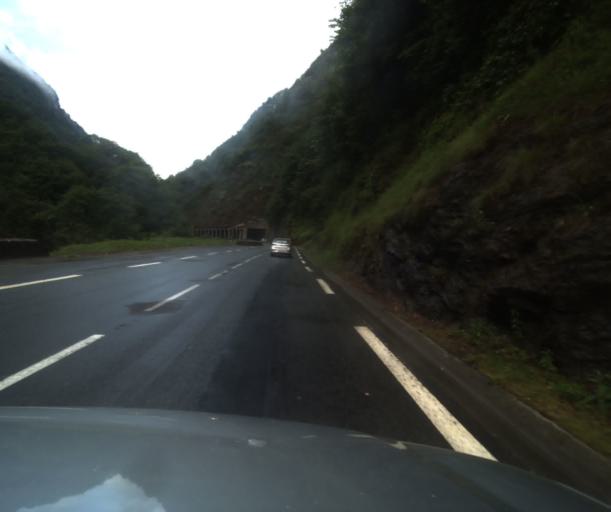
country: FR
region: Midi-Pyrenees
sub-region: Departement des Hautes-Pyrenees
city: Pierrefitte-Nestalas
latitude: 42.9272
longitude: -0.0417
